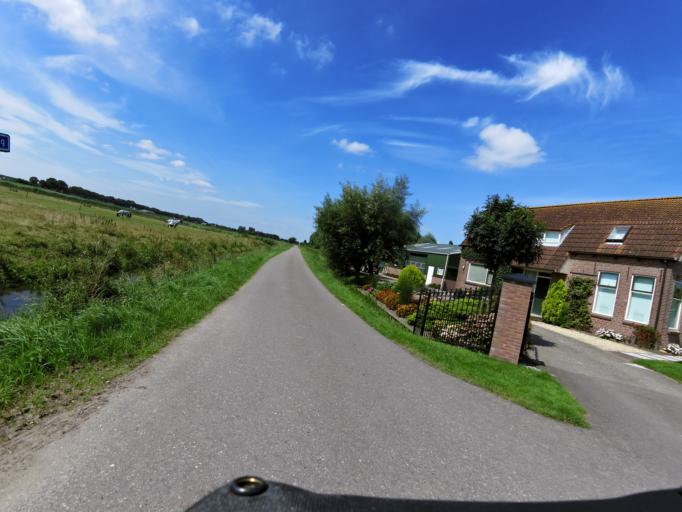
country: NL
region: South Holland
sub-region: Gemeente Binnenmaas
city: Heinenoord
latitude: 51.8495
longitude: 4.4779
